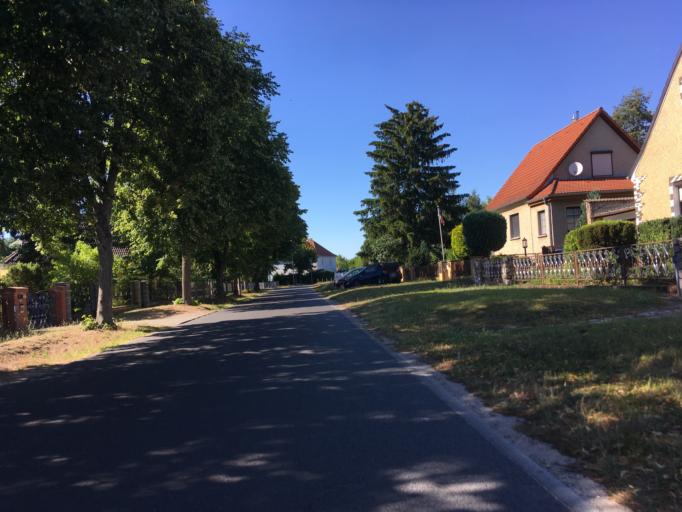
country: DE
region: Brandenburg
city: Schulzendorf
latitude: 52.3698
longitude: 13.5946
